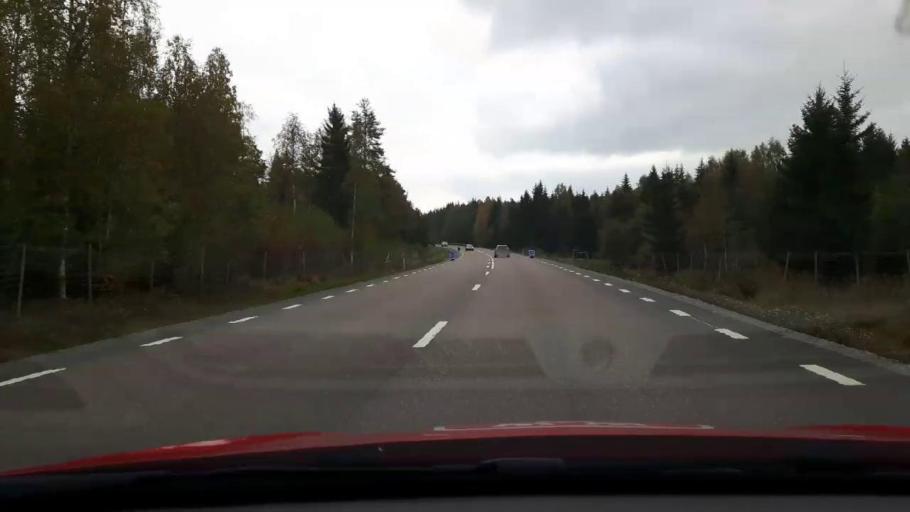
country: SE
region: Gaevleborg
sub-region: Bollnas Kommun
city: Bollnas
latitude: 61.3017
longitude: 16.4711
